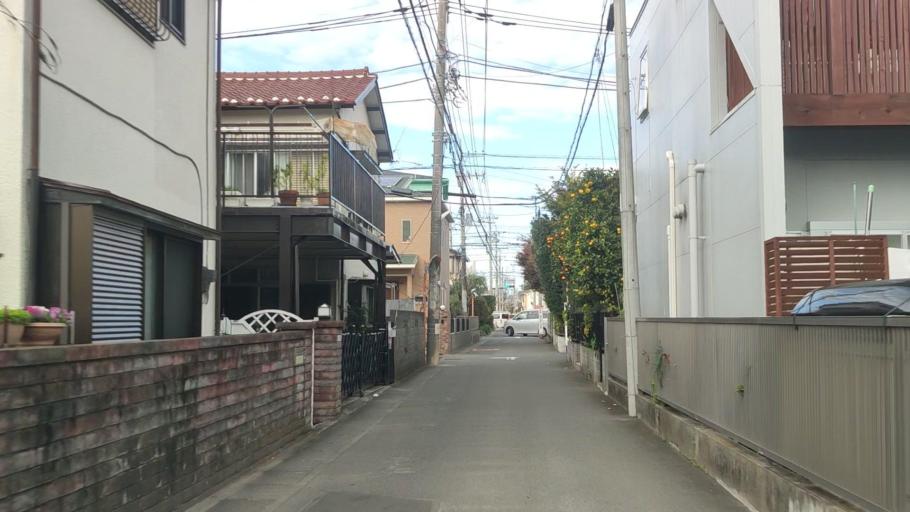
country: JP
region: Kanagawa
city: Minami-rinkan
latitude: 35.4902
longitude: 139.4376
